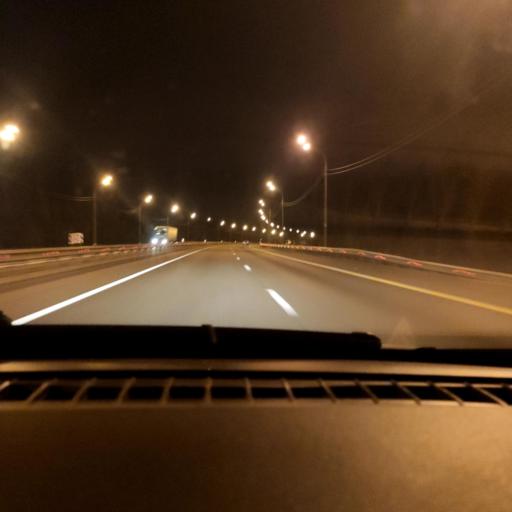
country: RU
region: Lipetsk
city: Khlevnoye
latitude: 52.2577
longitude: 39.0652
